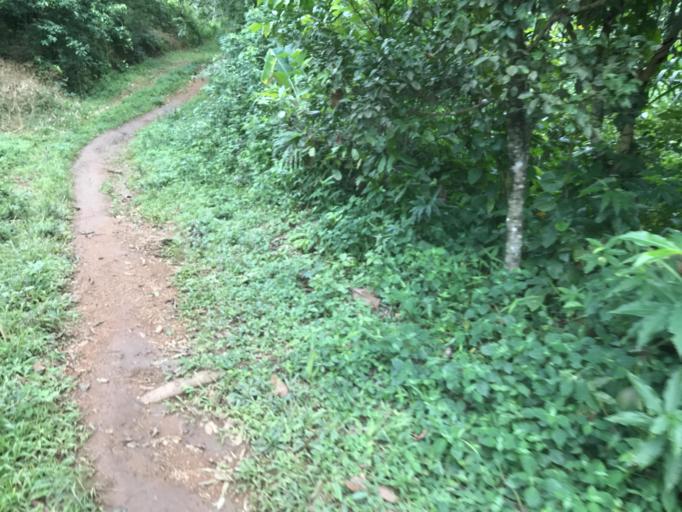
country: GN
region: Nzerekore
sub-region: Prefecture de Guekedou
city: Gueckedou
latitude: 8.4720
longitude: -10.3092
